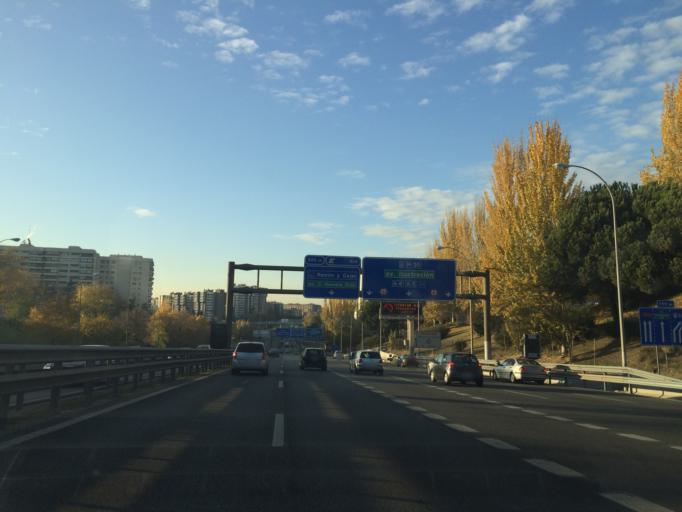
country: ES
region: Madrid
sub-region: Provincia de Madrid
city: Pinar de Chamartin
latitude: 40.4838
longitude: -3.6891
